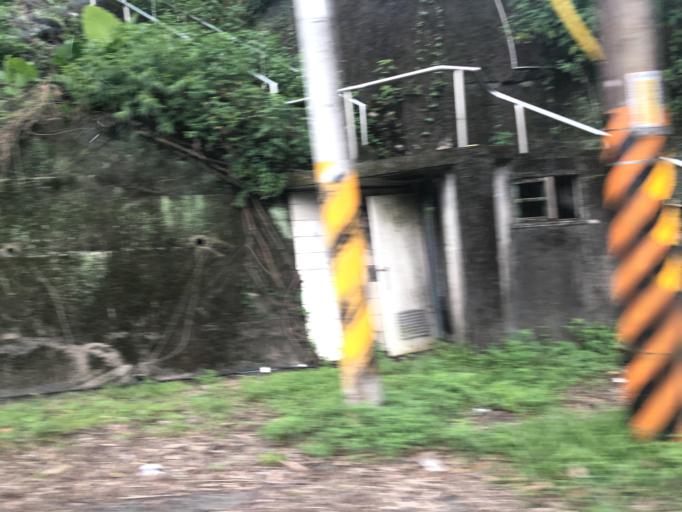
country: TW
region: Taiwan
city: Daxi
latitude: 24.9123
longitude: 121.3869
